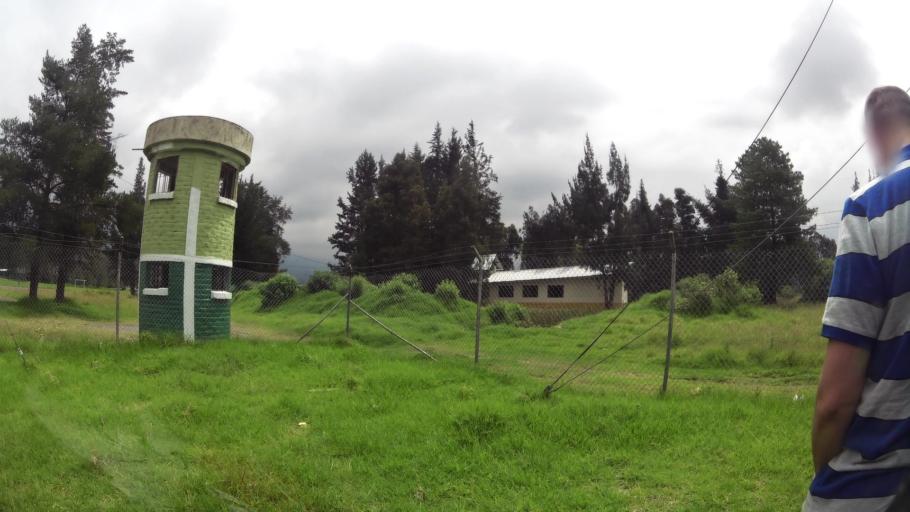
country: EC
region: Pichincha
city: Sangolqui
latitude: -0.3491
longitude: -78.4743
